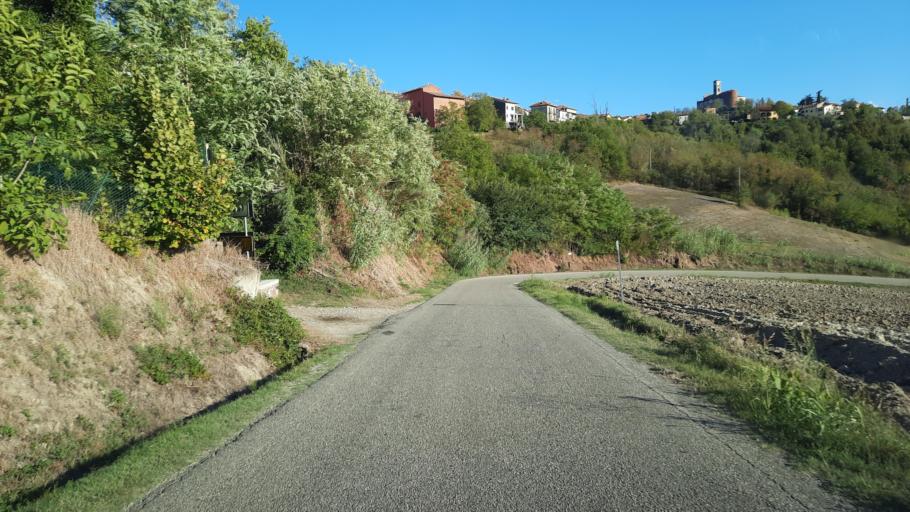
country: IT
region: Piedmont
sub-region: Provincia di Alessandria
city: Cuccaro Monferrato
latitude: 44.9955
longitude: 8.4533
